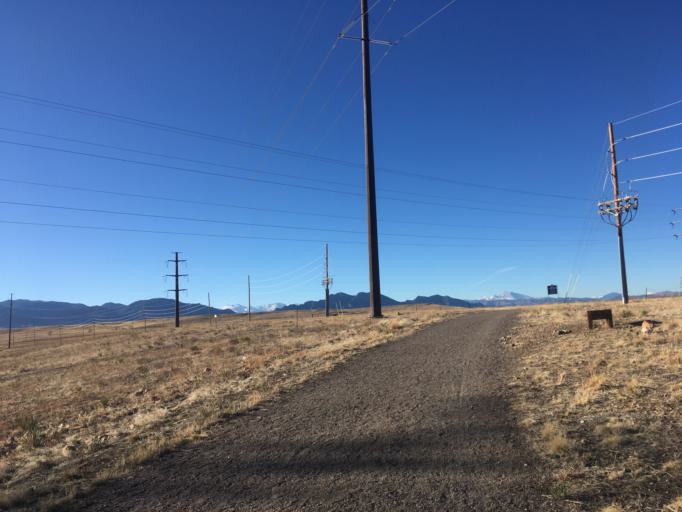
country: US
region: Colorado
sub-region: Boulder County
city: Superior
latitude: 39.8903
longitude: -105.1576
